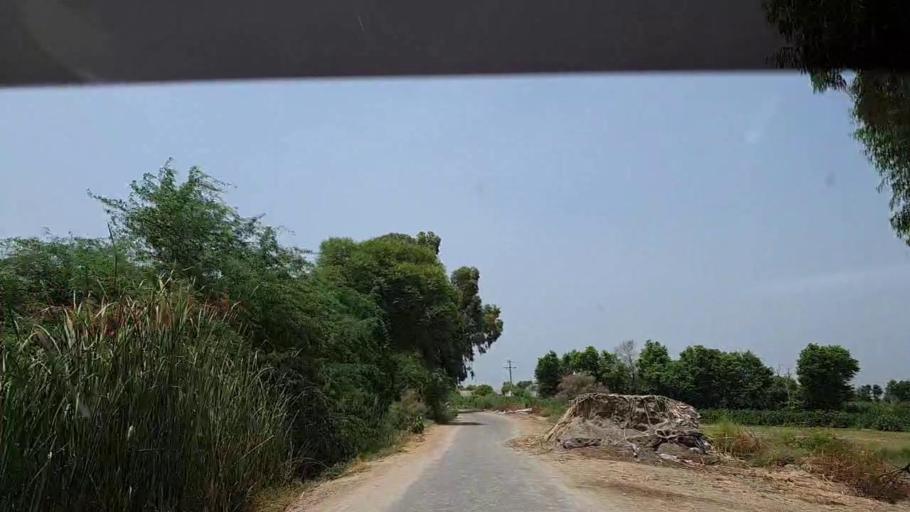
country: PK
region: Sindh
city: Adilpur
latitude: 27.8777
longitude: 69.2684
